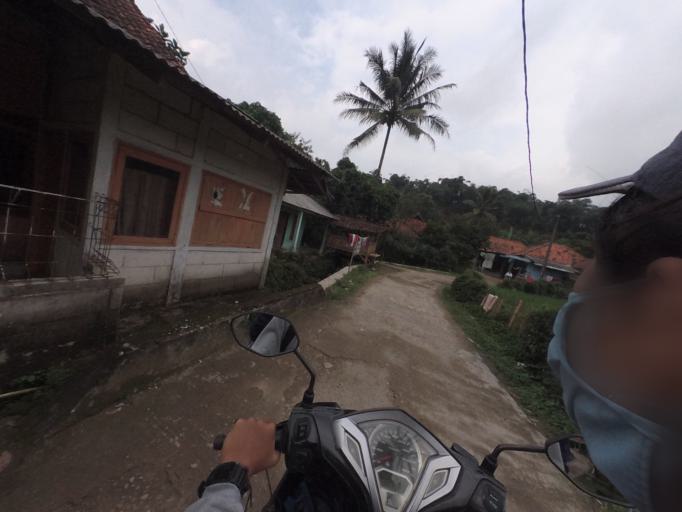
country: ID
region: West Java
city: Ciampea
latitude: -6.6842
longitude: 106.6598
